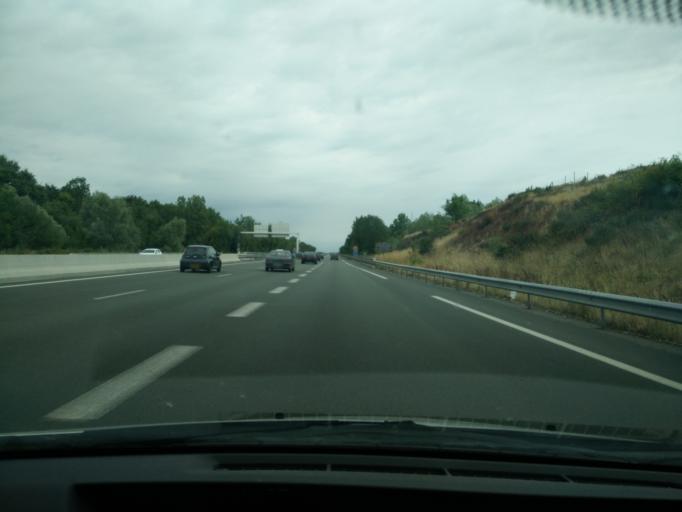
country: FR
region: Pays de la Loire
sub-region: Departement de Maine-et-Loire
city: Les Ponts-de-Ce
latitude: 47.4049
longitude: -0.5098
